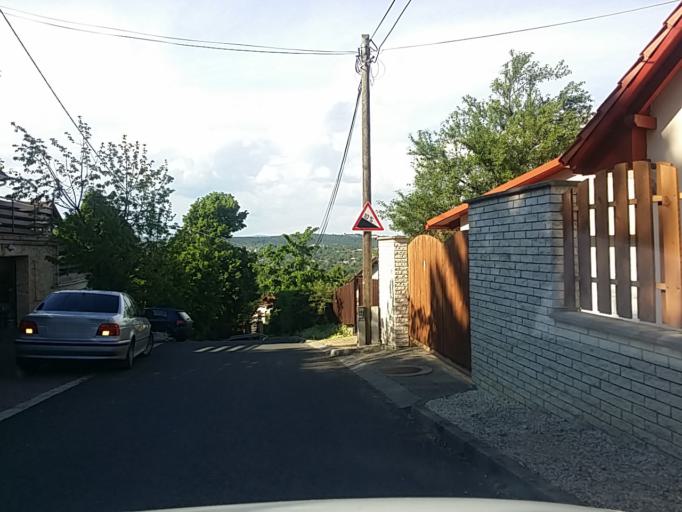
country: HU
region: Budapest
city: Budapest III. keruelet
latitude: 47.5579
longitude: 19.0180
